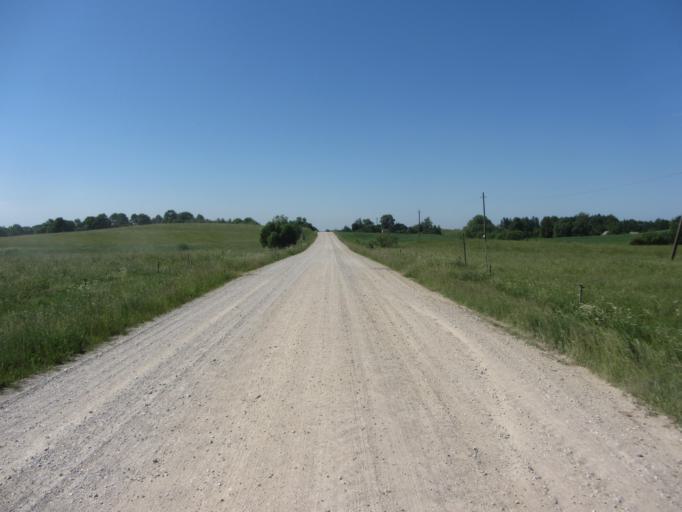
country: LT
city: Ziezmariai
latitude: 54.7329
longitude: 24.3044
